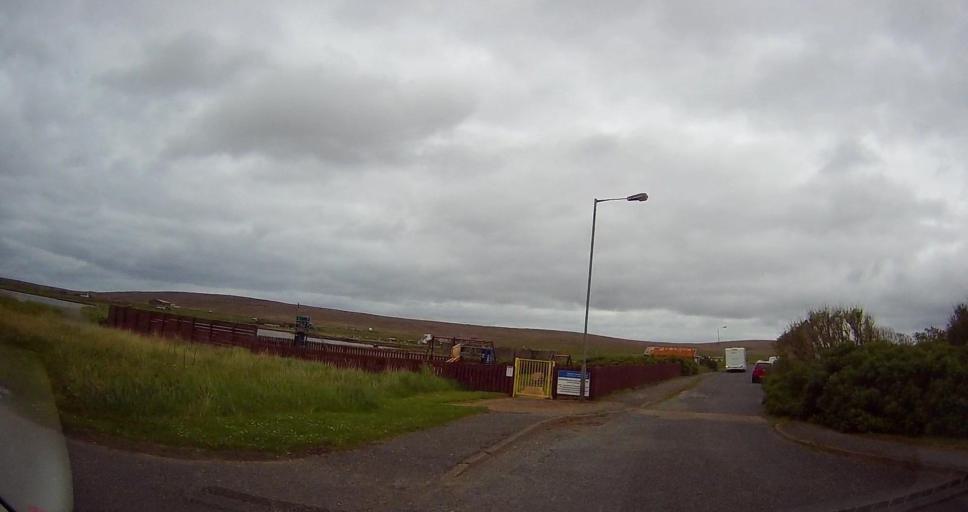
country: GB
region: Scotland
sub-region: Shetland Islands
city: Shetland
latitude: 60.7582
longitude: -0.8593
